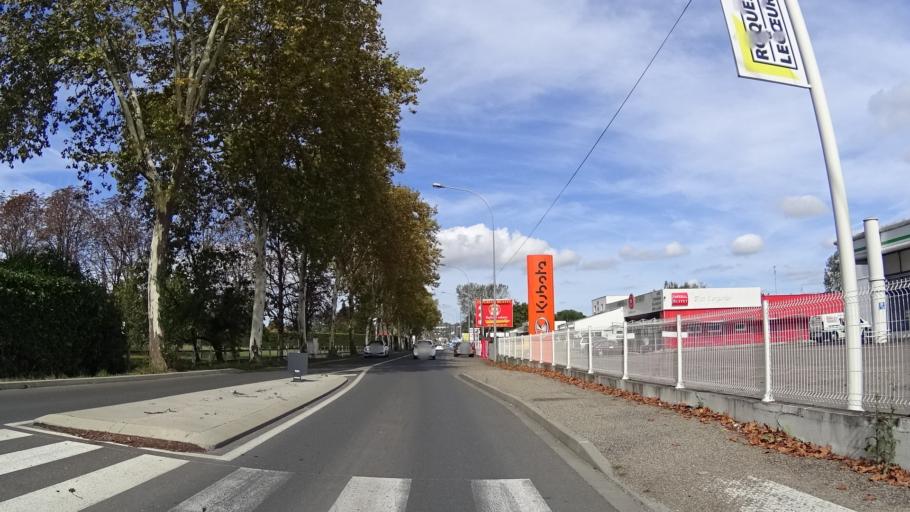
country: FR
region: Aquitaine
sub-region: Departement du Lot-et-Garonne
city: Agen
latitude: 44.1854
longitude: 0.6322
